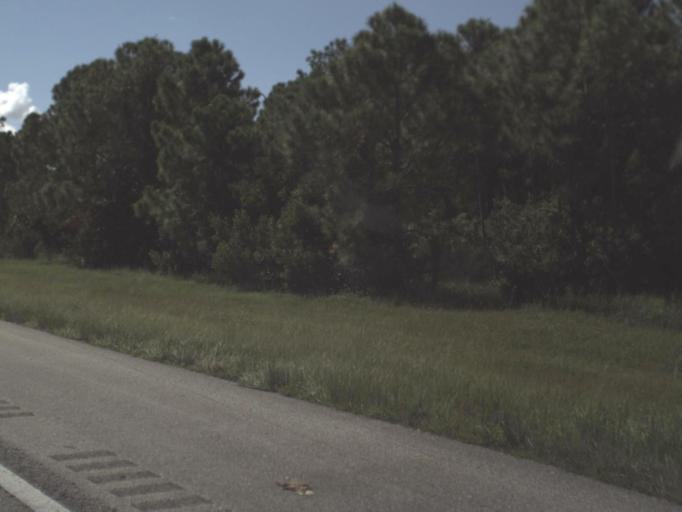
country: US
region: Florida
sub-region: Lee County
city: Suncoast Estates
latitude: 26.8122
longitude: -81.9340
